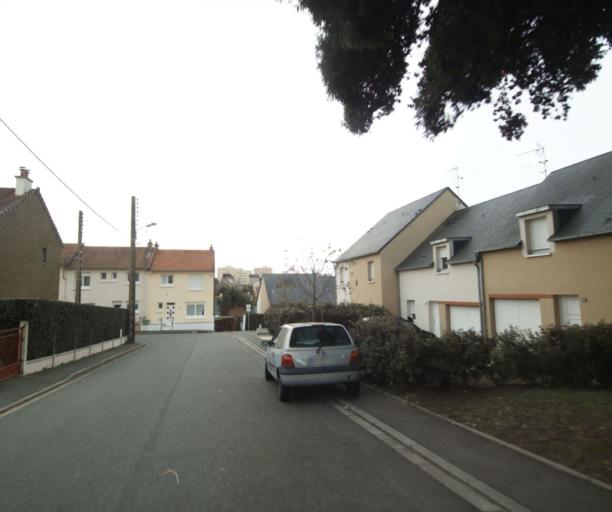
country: FR
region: Pays de la Loire
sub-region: Departement de la Sarthe
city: Coulaines
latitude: 48.0118
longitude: 0.2154
